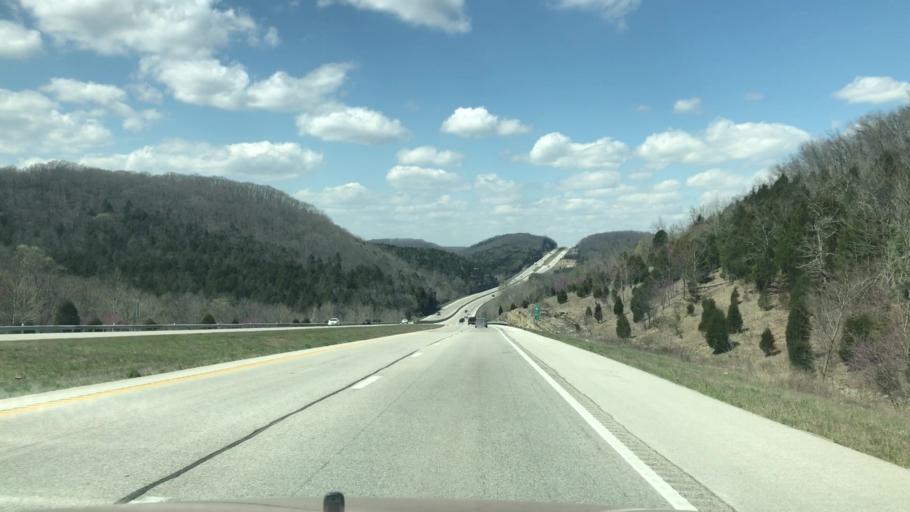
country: US
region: Missouri
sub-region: Taney County
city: Merriam Woods
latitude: 36.8535
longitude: -93.2237
